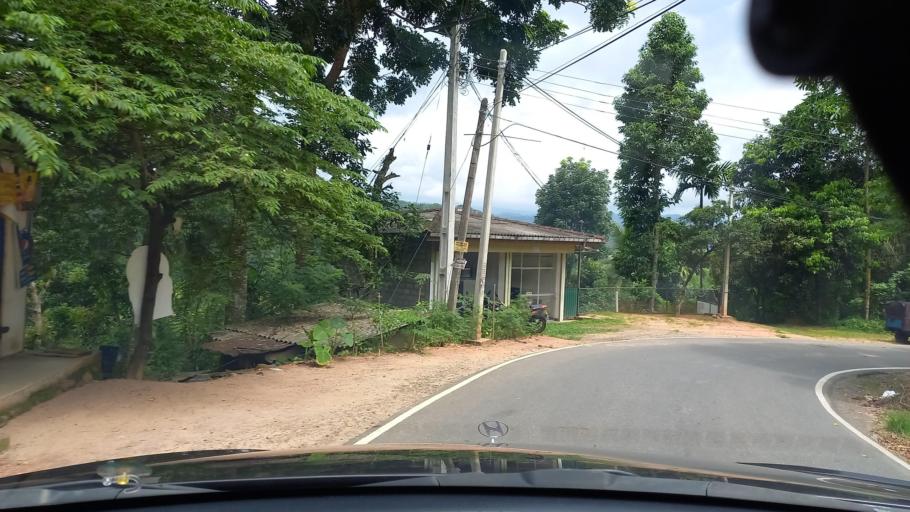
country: LK
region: Central
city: Gampola
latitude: 7.2172
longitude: 80.6124
